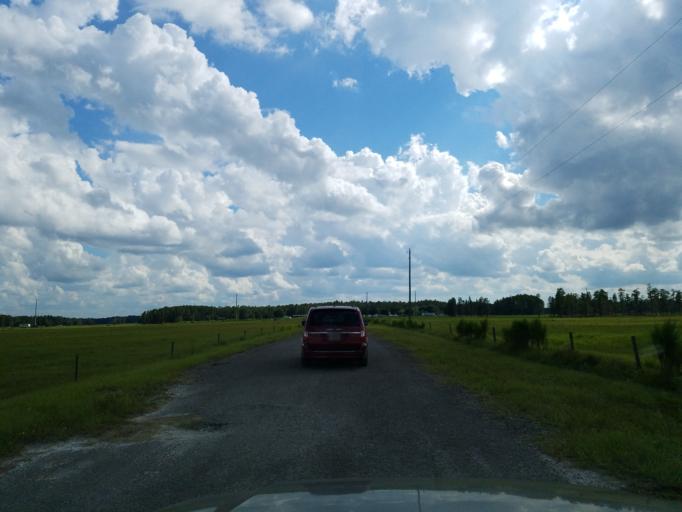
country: US
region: Florida
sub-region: Pasco County
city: Wesley Chapel
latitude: 28.3274
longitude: -82.3980
